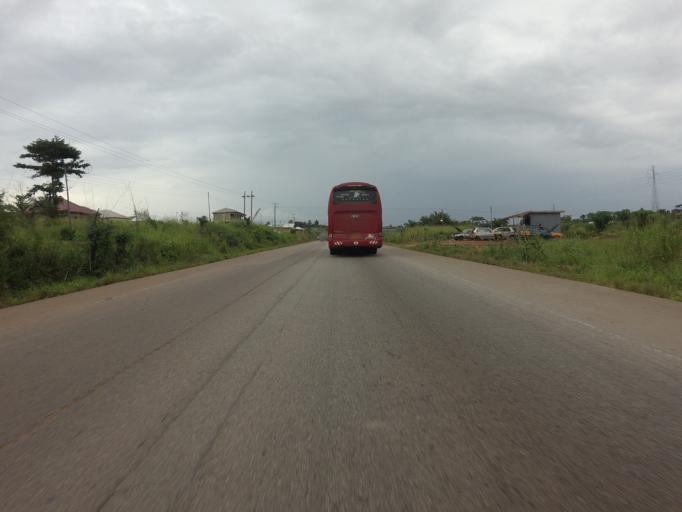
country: GH
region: Ashanti
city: Konongo
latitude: 6.6169
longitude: -1.1763
